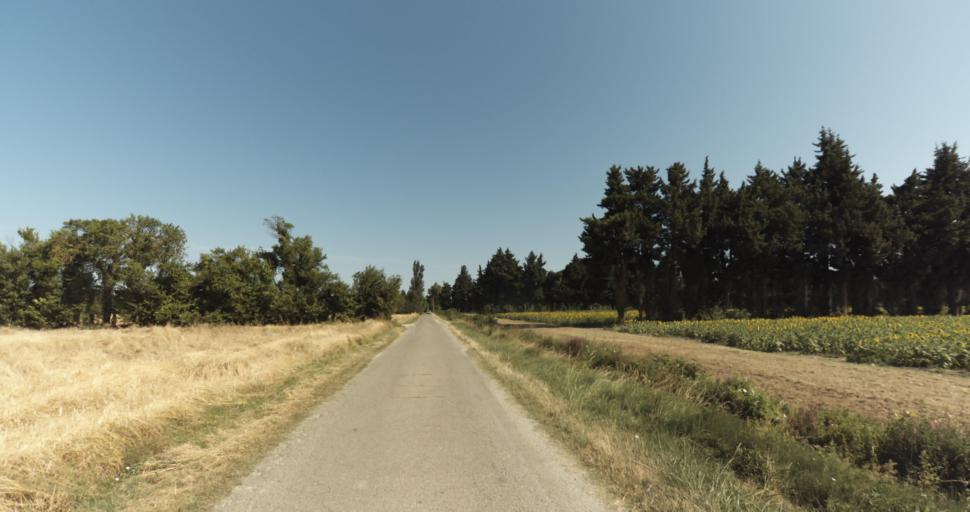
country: FR
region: Provence-Alpes-Cote d'Azur
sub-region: Departement du Vaucluse
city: Althen-des-Paluds
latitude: 44.0086
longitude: 4.9738
